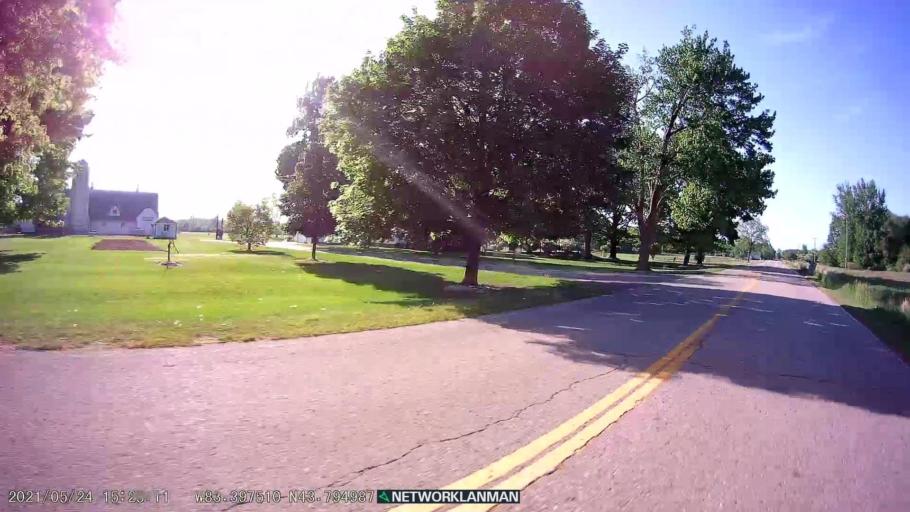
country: US
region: Michigan
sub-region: Huron County
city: Kilmanagh
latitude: 43.7954
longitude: -83.3974
